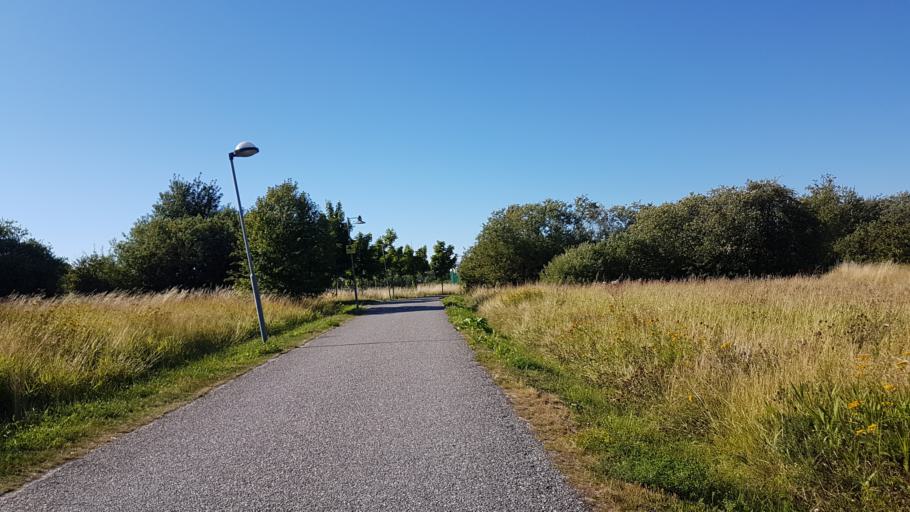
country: SE
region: Stockholm
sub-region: Stockholms Kommun
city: Arsta
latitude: 59.2898
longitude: 18.0426
